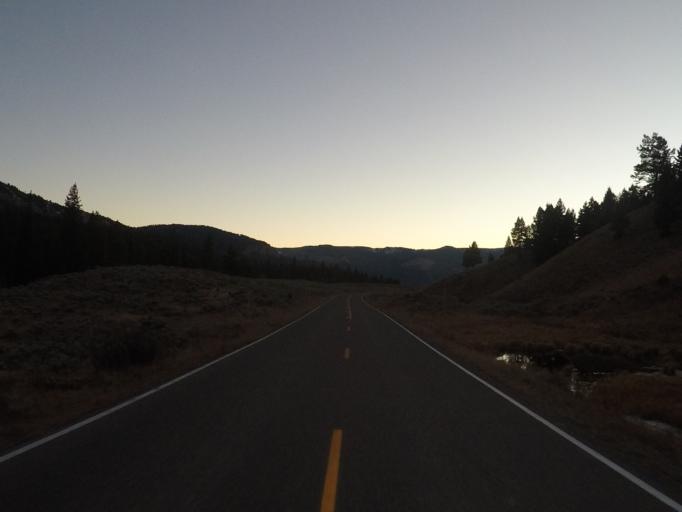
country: US
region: Montana
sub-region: Park County
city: Livingston
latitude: 44.8980
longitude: -110.1242
